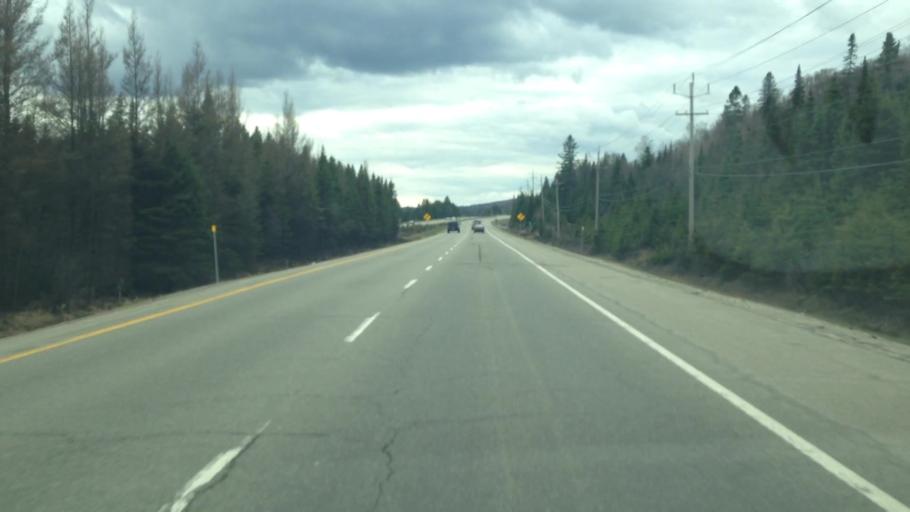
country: CA
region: Quebec
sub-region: Laurentides
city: Sainte-Agathe-des-Monts
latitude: 46.0910
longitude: -74.3346
